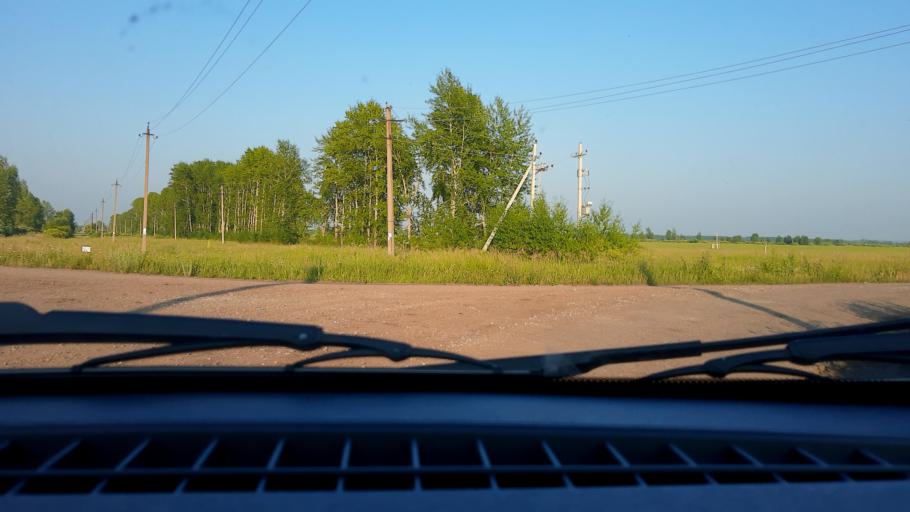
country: RU
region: Bashkortostan
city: Asanovo
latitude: 54.9337
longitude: 55.6240
